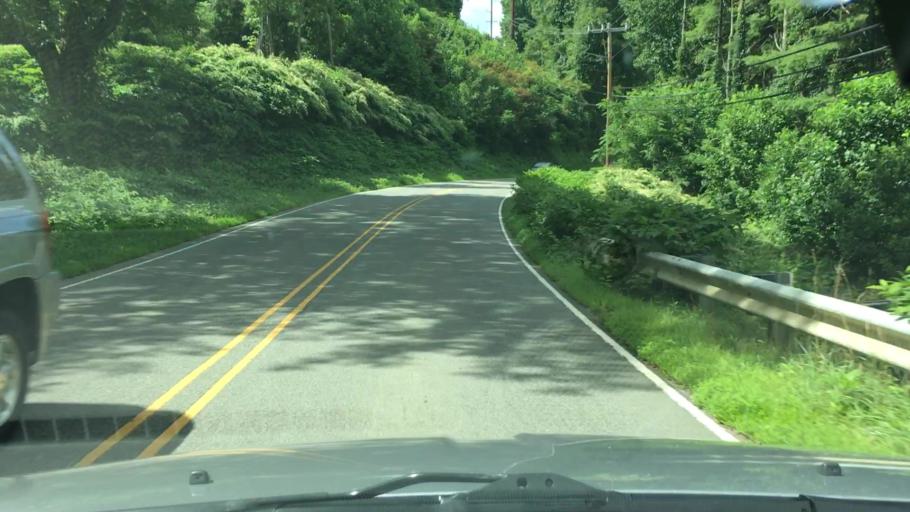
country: US
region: North Carolina
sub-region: Yancey County
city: Burnsville
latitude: 35.8656
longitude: -82.2031
